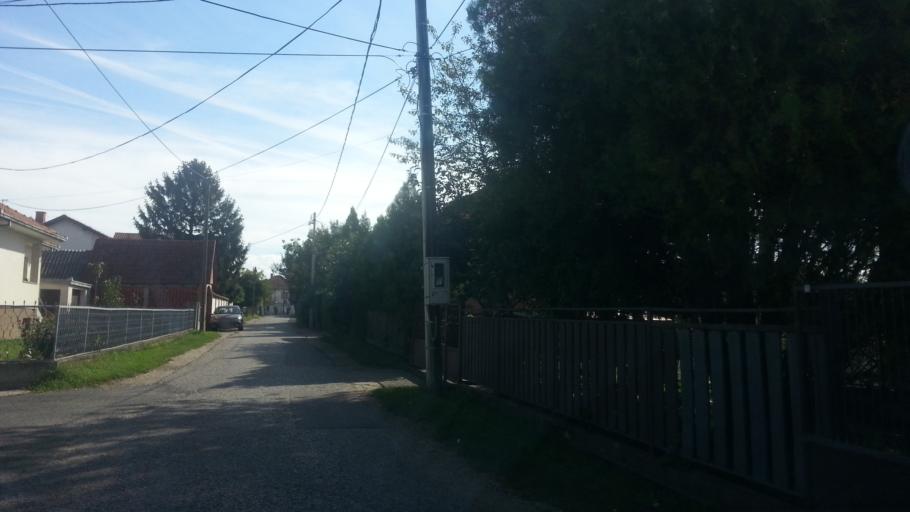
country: RS
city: Novi Banovci
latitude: 44.9627
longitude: 20.2794
